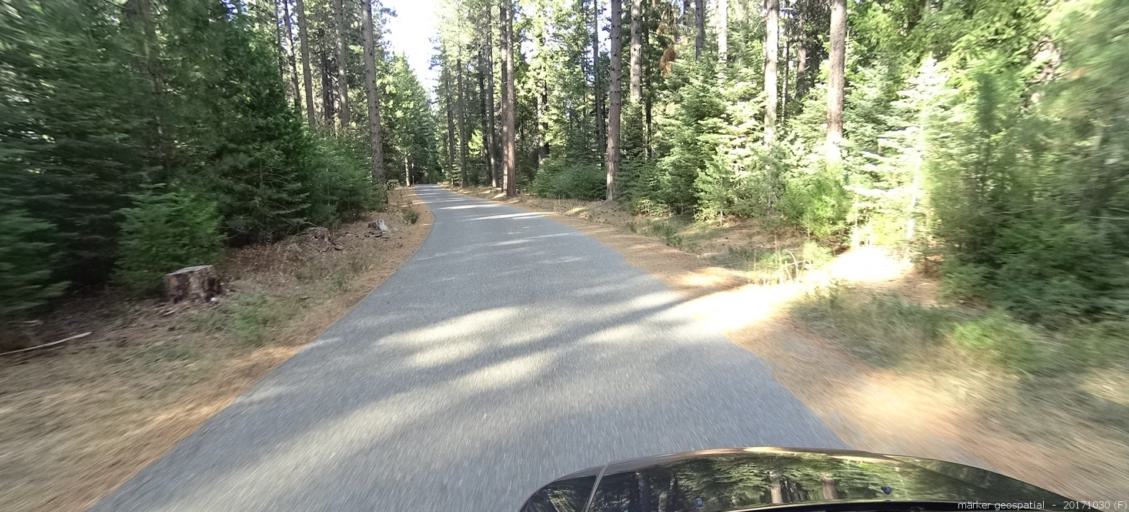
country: US
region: California
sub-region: Shasta County
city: Shingletown
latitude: 40.5215
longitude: -121.6881
